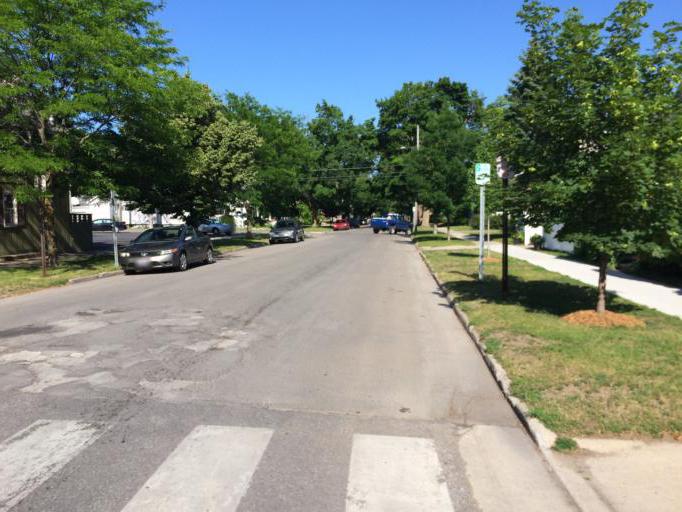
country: US
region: Michigan
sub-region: Grand Traverse County
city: Traverse City
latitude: 44.7582
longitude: -85.6238
